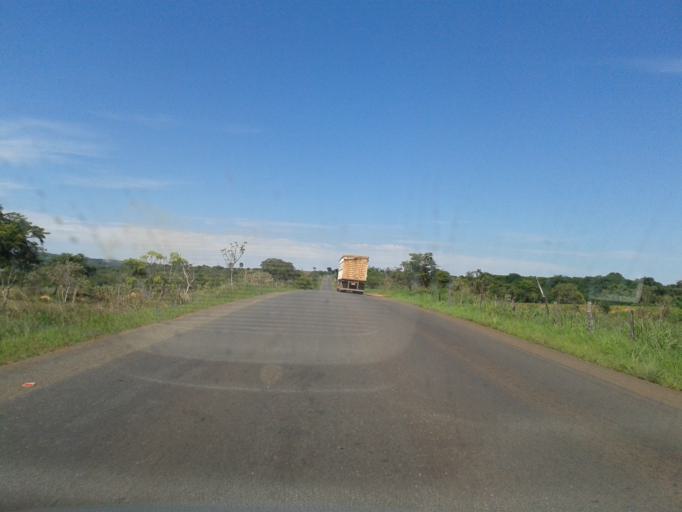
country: BR
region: Goias
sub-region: Bela Vista De Goias
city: Bela Vista de Goias
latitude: -17.1692
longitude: -48.7361
